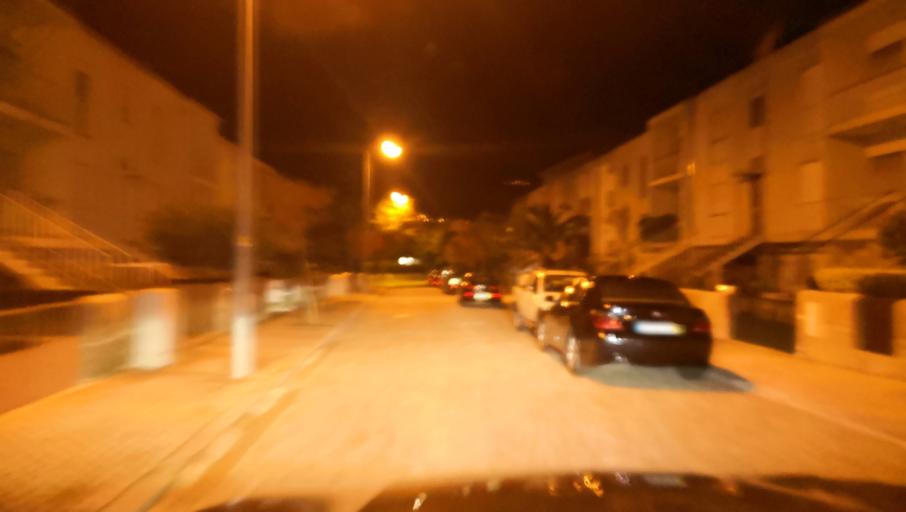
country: PT
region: Vila Real
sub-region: Vila Real
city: Vila Real
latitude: 41.3022
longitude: -7.7463
